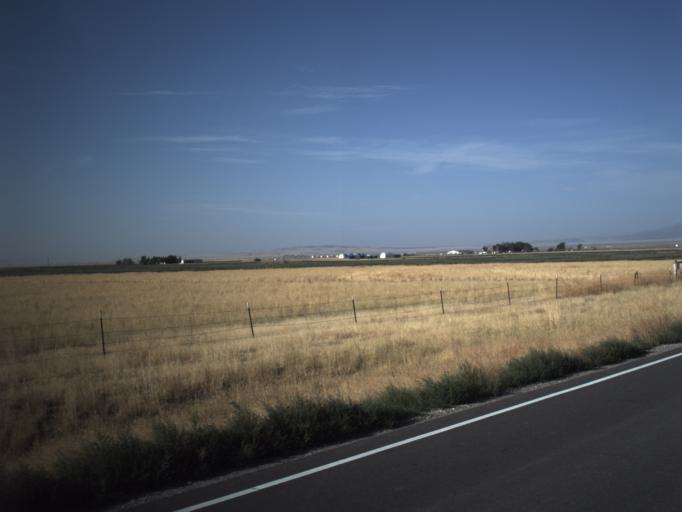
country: US
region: Idaho
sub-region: Oneida County
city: Malad City
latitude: 41.9674
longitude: -112.8230
